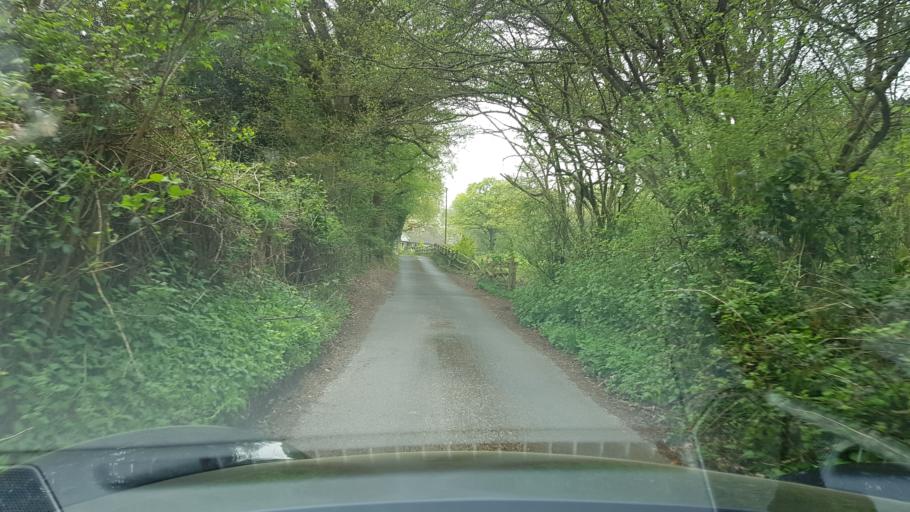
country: GB
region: England
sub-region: Surrey
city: East Horsley
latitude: 51.2425
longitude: -0.4493
